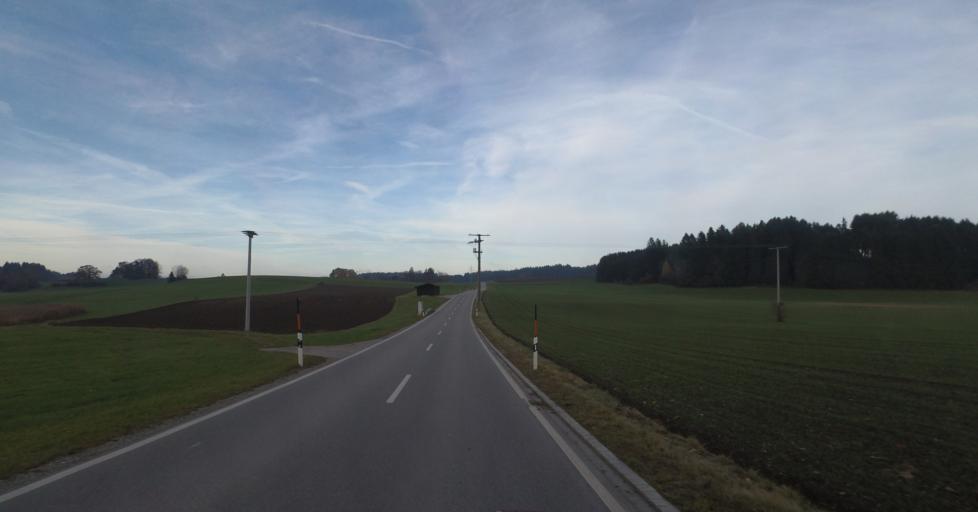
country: DE
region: Bavaria
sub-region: Upper Bavaria
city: Nussdorf
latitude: 47.8816
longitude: 12.6094
